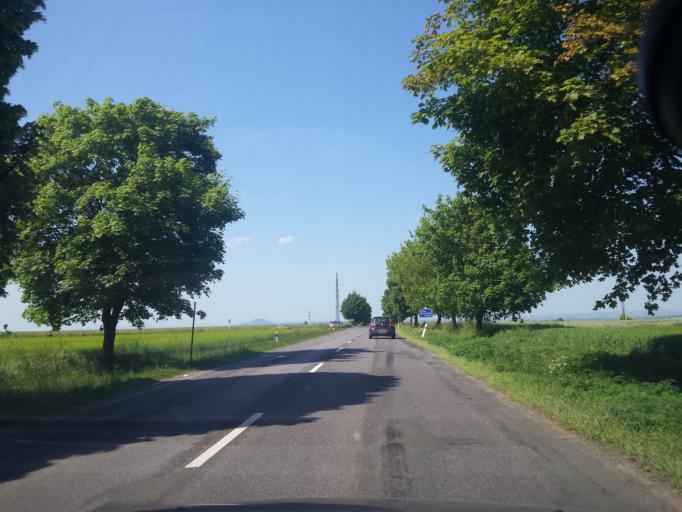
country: CZ
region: Central Bohemia
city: Kralupy nad Vltavou
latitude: 50.2105
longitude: 14.3162
